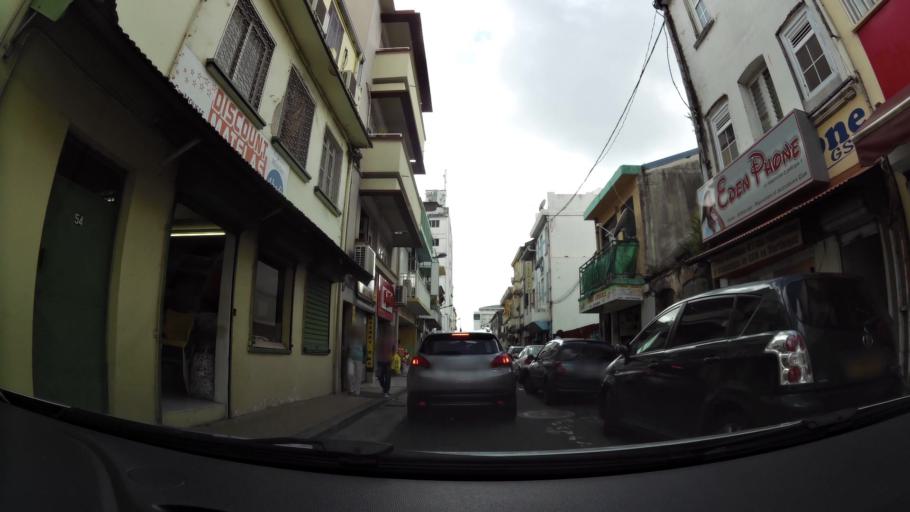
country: MQ
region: Martinique
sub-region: Martinique
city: Fort-de-France
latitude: 14.6051
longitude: -61.0726
